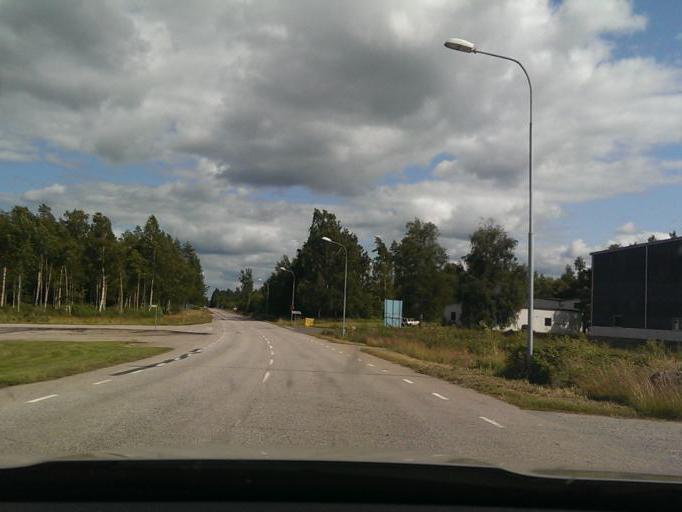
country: SE
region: Kronoberg
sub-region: Ljungby Kommun
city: Lagan
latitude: 56.9676
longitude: 13.9502
